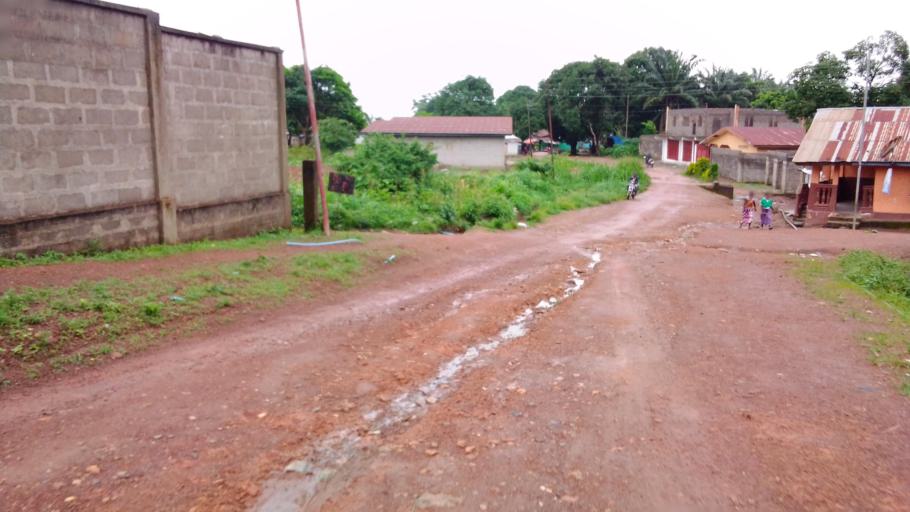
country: SL
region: Eastern Province
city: Kenema
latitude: 7.8996
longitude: -11.1860
